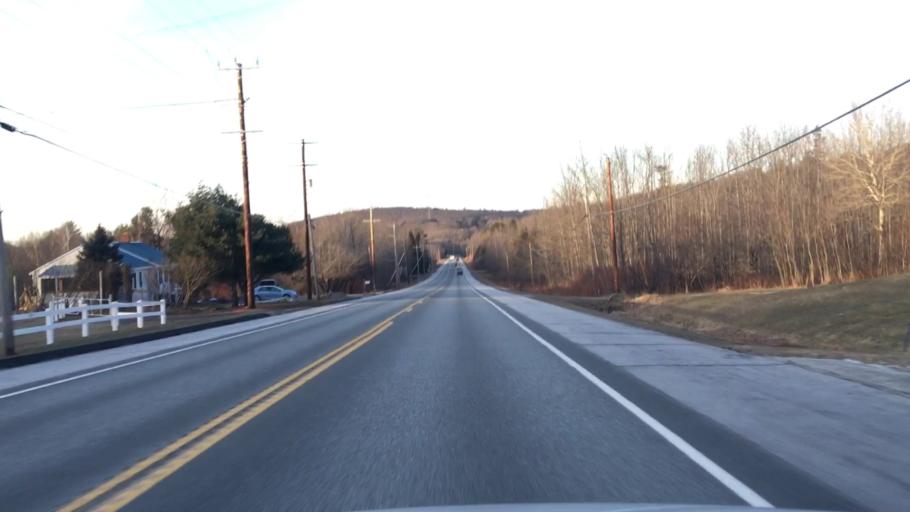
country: US
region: Maine
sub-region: Hancock County
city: Dedham
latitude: 44.7061
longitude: -68.6004
